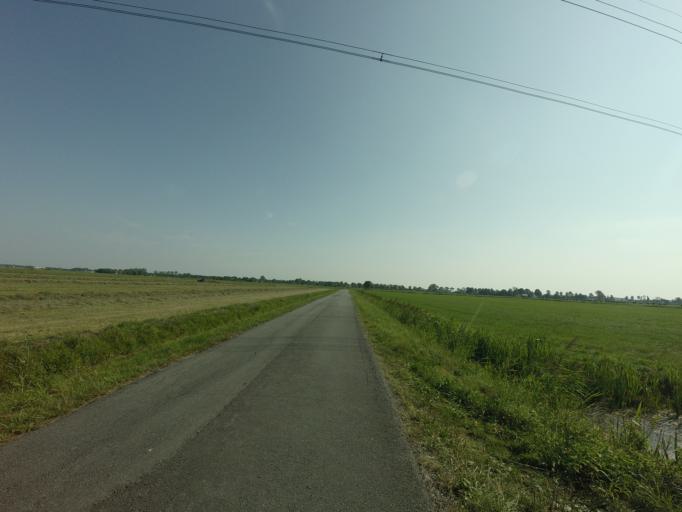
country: NL
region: Groningen
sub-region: Gemeente Zuidhorn
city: Zuidhorn
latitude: 53.2170
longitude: 6.4310
